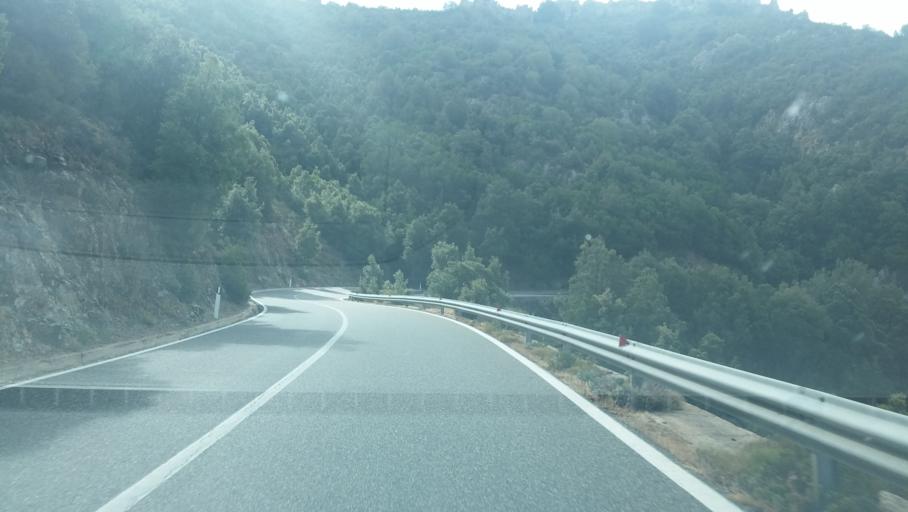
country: IT
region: Sardinia
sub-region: Provincia di Ogliastra
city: Urzulei
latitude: 40.1869
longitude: 9.5356
